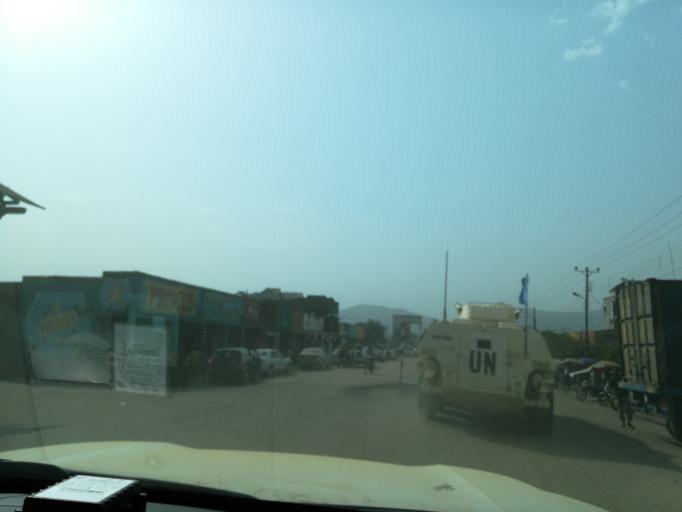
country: UG
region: Western Region
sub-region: Kasese District
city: Kilembe
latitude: 0.0415
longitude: 29.7155
